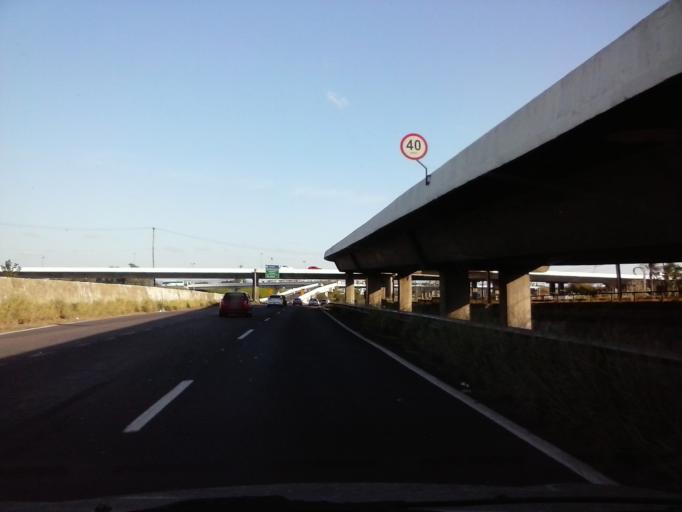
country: BR
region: Rio Grande do Sul
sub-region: Canoas
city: Canoas
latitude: -29.9683
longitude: -51.1764
